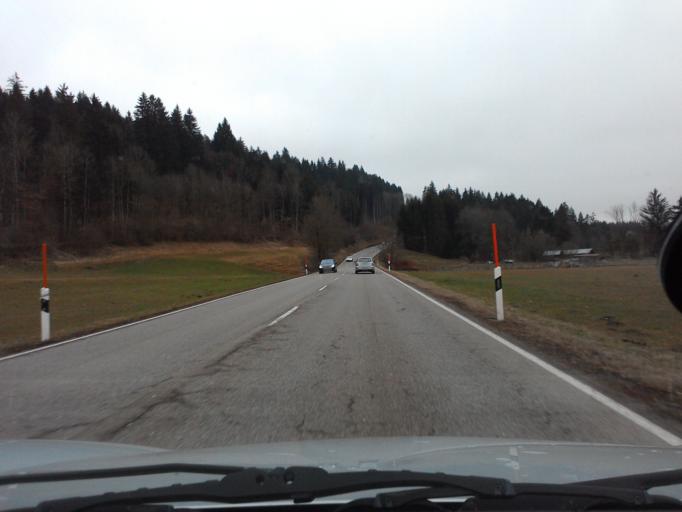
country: DE
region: Bavaria
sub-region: Swabia
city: Bolsterlang
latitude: 47.4747
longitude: 10.2673
